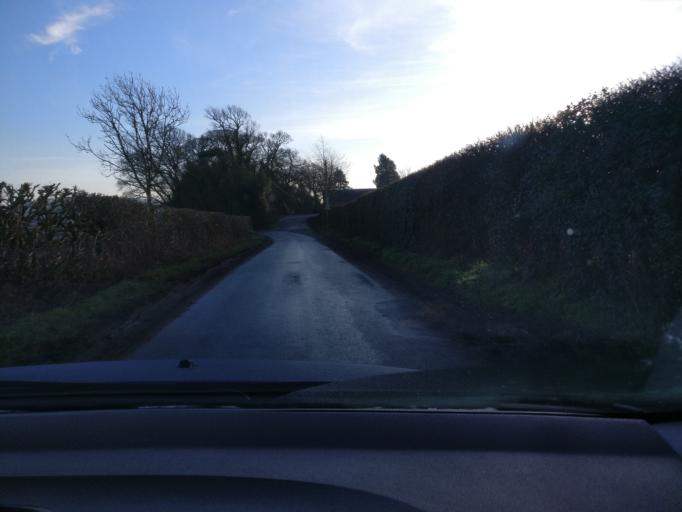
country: GB
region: Scotland
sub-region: The Scottish Borders
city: Hawick
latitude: 55.4464
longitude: -2.7570
